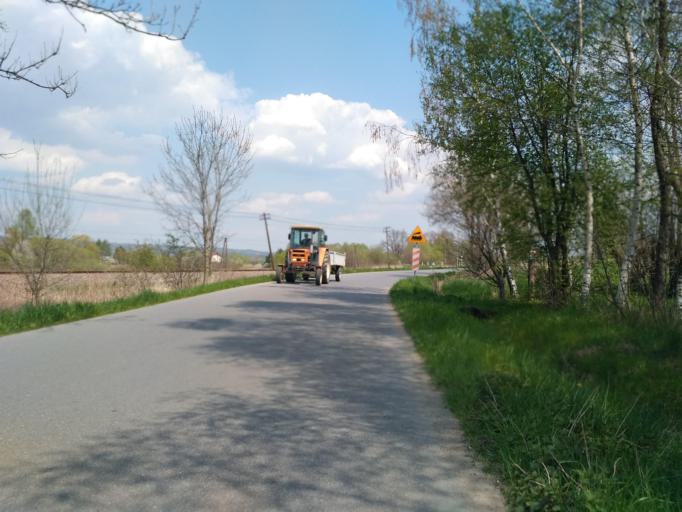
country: PL
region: Subcarpathian Voivodeship
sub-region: Powiat jasielski
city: Jaslo
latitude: 49.7356
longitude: 21.5208
